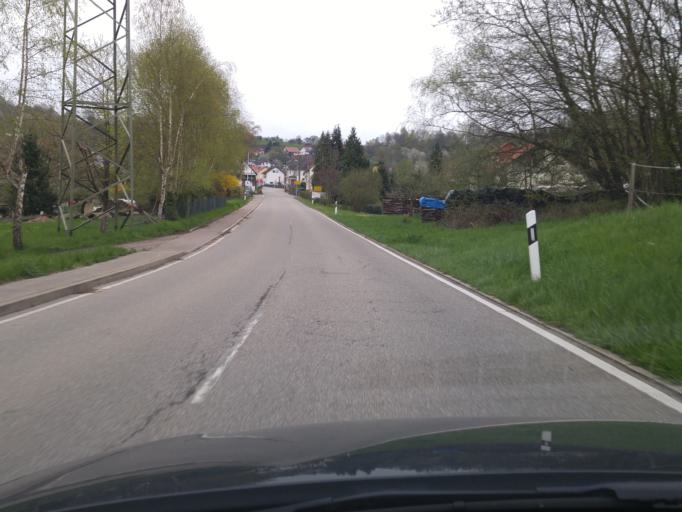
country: DE
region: Hesse
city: Neckarsteinach
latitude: 49.3896
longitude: 8.8520
